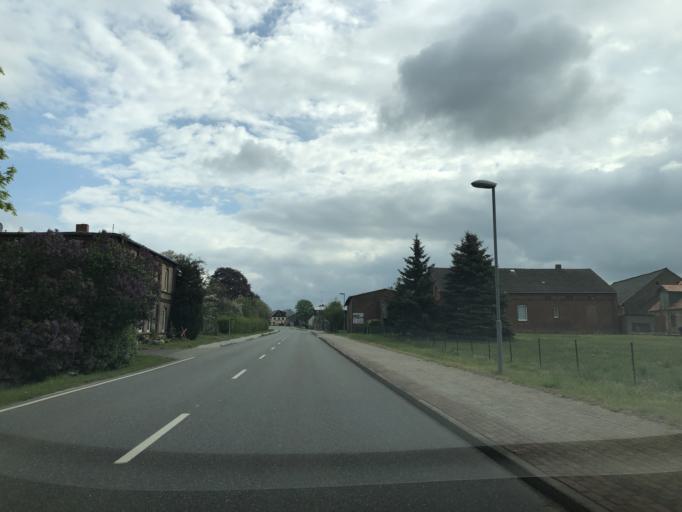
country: DE
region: Mecklenburg-Vorpommern
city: Plau am See
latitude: 53.4642
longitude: 12.1747
